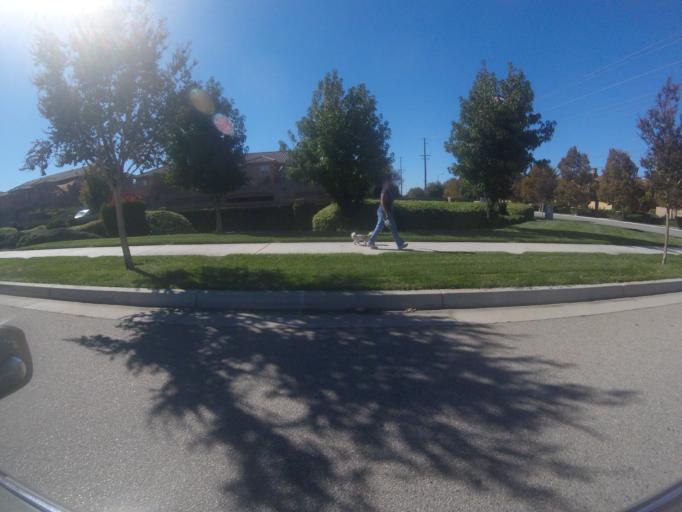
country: US
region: California
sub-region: San Bernardino County
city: Redlands
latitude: 34.0516
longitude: -117.2174
